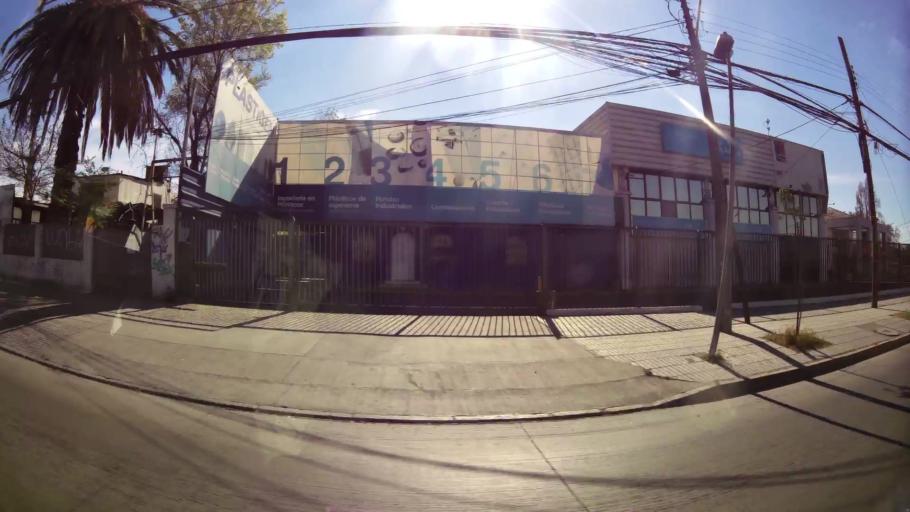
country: CL
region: Santiago Metropolitan
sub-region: Provincia de Santiago
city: Lo Prado
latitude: -33.5016
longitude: -70.7105
